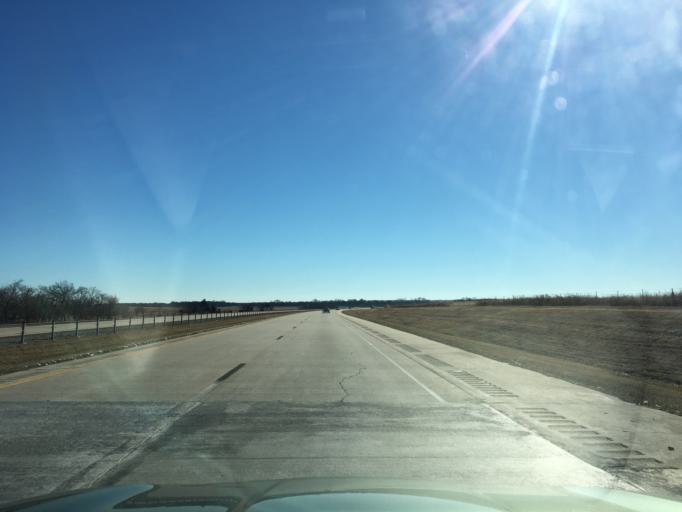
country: US
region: Oklahoma
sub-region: Kay County
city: Tonkawa
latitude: 36.4914
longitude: -97.3301
